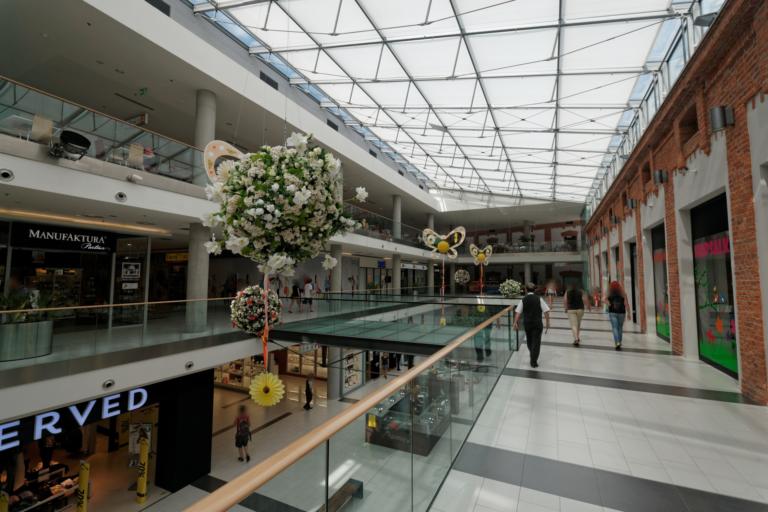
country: CZ
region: Moravskoslezsky
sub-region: Okres Opava
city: Opava
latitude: 49.9407
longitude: 17.8997
